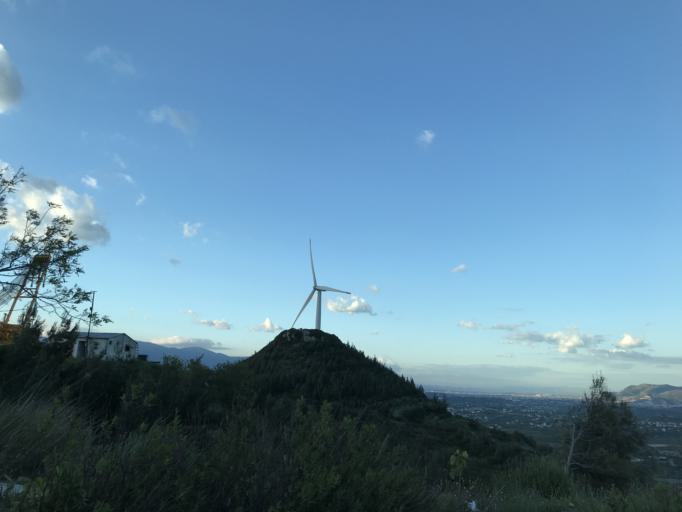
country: TR
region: Hatay
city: Buyukcat
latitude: 36.1100
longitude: 36.0481
